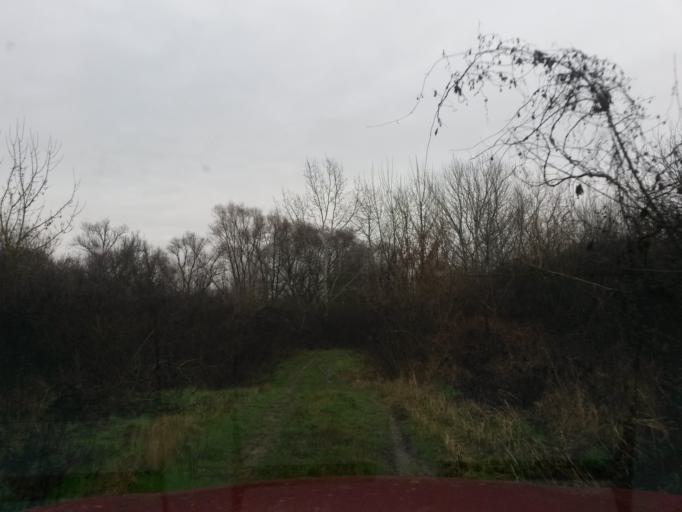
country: UA
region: Zakarpattia
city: Storozhnytsya
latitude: 48.6281
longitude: 22.1069
